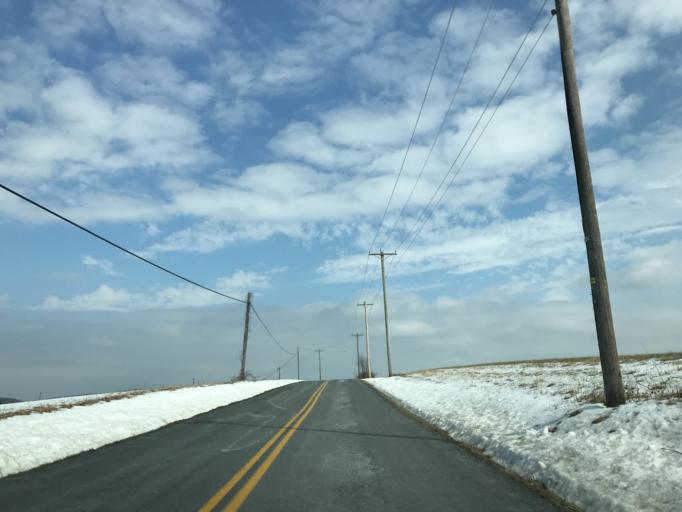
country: US
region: Maryland
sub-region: Harford County
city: Bel Air North
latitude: 39.6506
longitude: -76.3409
